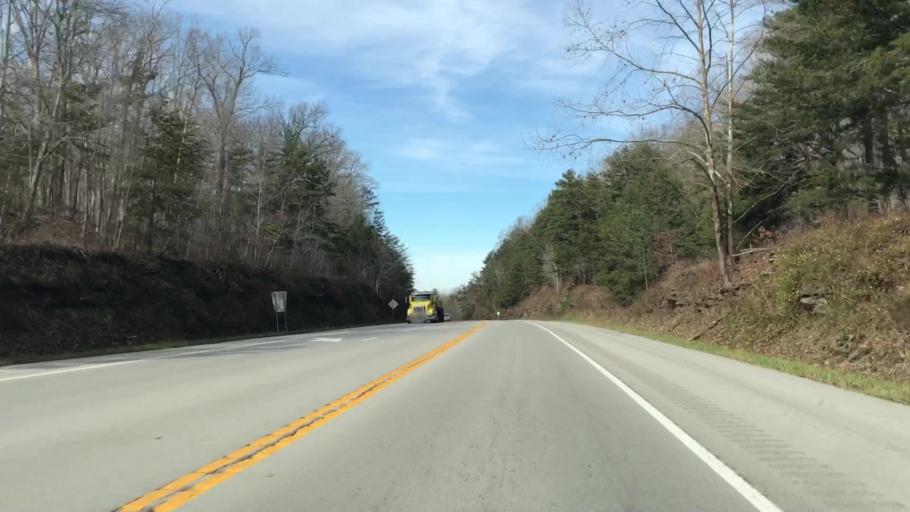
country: US
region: Kentucky
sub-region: McCreary County
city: Whitley City
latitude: 36.8969
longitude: -84.4956
